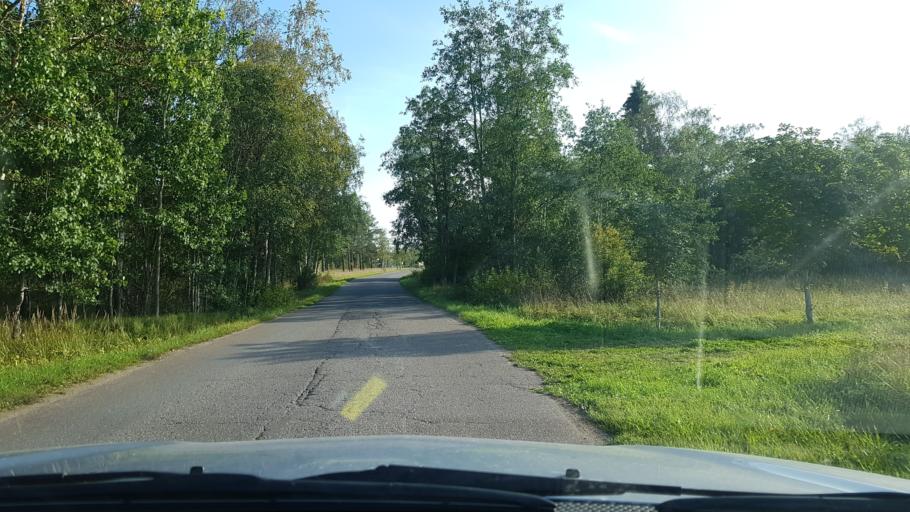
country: EE
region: Ida-Virumaa
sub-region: Narva-Joesuu linn
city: Narva-Joesuu
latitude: 59.3858
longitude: 28.0885
